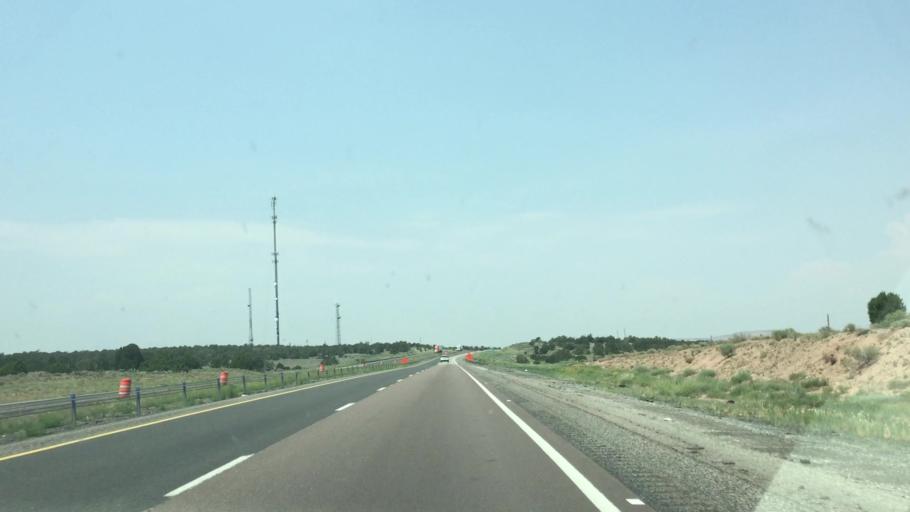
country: US
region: New Mexico
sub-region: McKinley County
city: Thoreau
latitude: 35.4637
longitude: -108.4041
